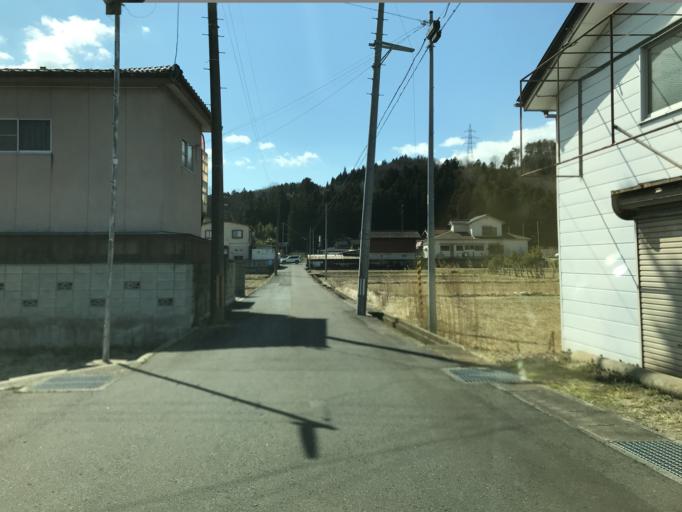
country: JP
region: Fukushima
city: Fukushima-shi
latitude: 37.7299
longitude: 140.4139
